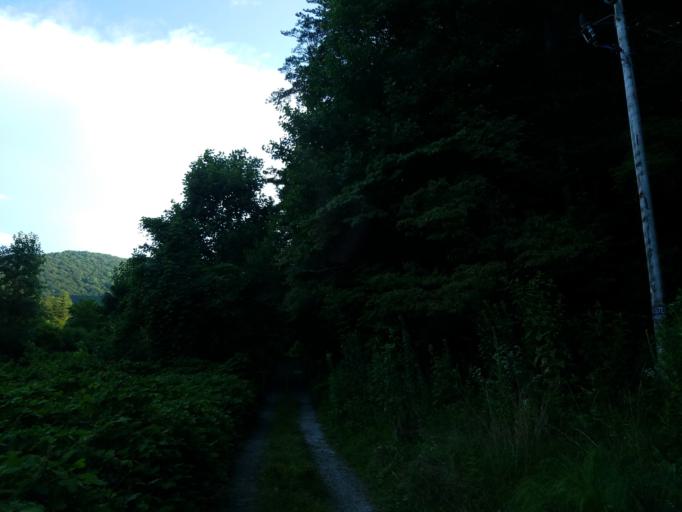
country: US
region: Georgia
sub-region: Lumpkin County
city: Dahlonega
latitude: 34.6659
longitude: -84.0863
